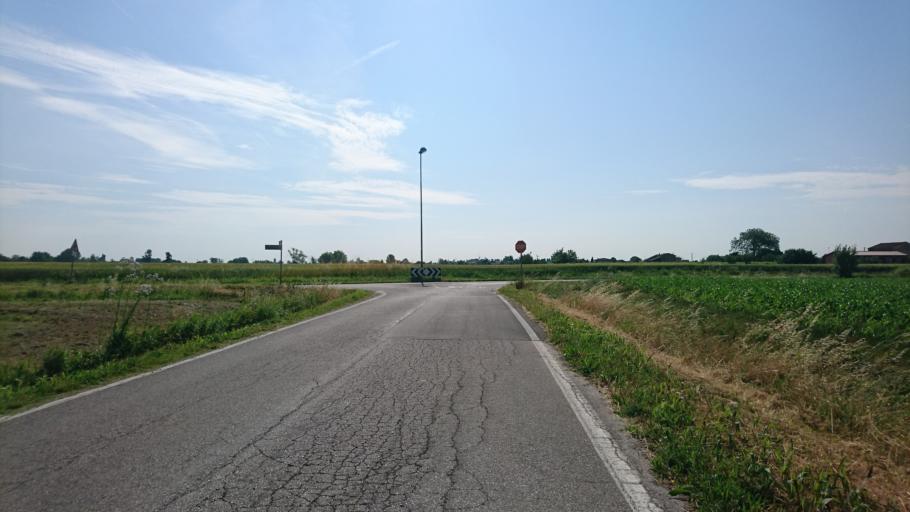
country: IT
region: Veneto
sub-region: Provincia di Padova
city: Merlara
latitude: 45.1698
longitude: 11.4491
